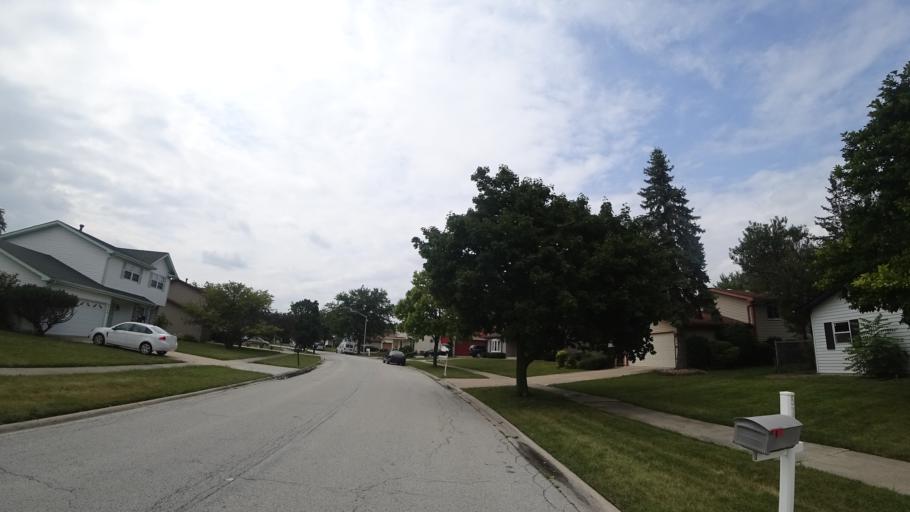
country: US
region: Illinois
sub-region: Will County
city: Frankfort Square
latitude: 41.5271
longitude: -87.7557
